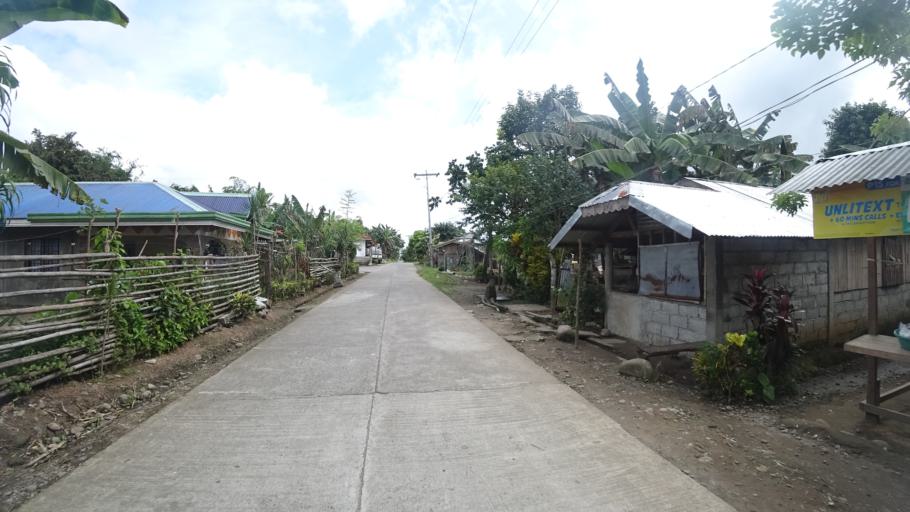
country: PH
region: Eastern Visayas
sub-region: Province of Leyte
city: Pastrana
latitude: 11.1736
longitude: 124.8718
